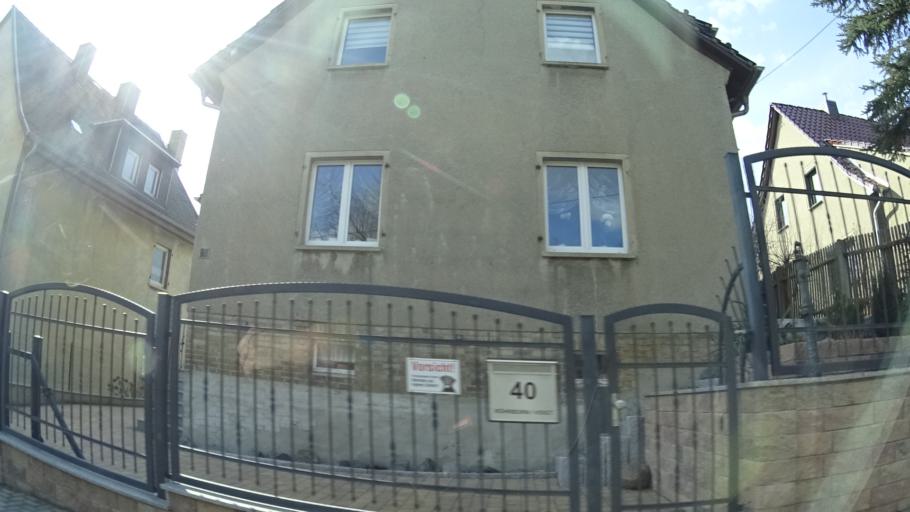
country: DE
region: Saxony-Anhalt
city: Prittitz
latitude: 51.1519
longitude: 11.9290
